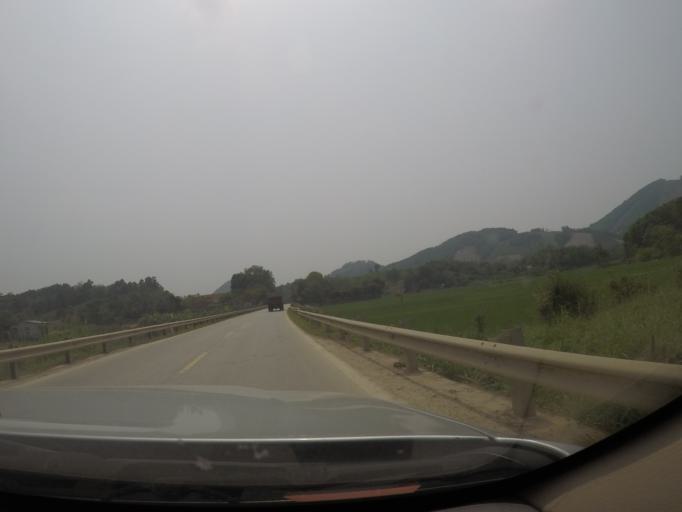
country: VN
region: Thanh Hoa
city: Thi Tran Yen Cat
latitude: 19.7324
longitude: 105.4268
